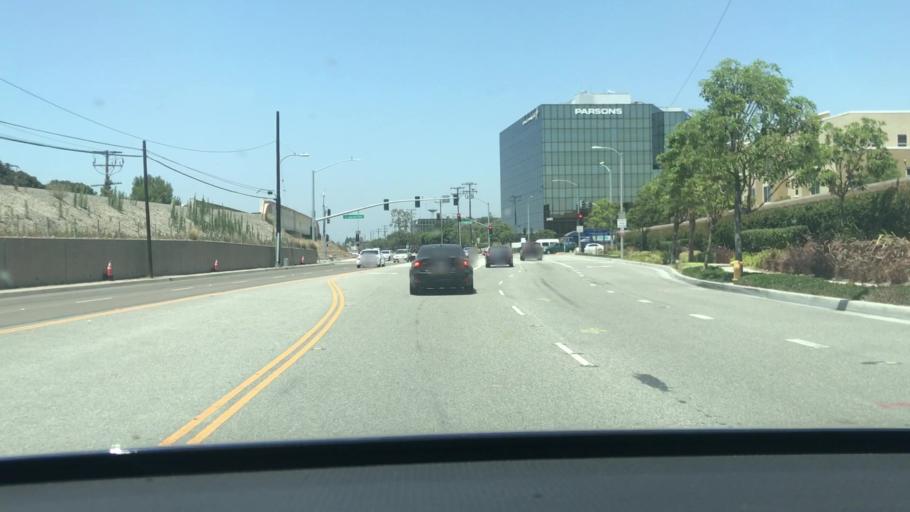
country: US
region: California
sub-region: Los Angeles County
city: Del Aire
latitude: 33.9153
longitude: -118.3786
